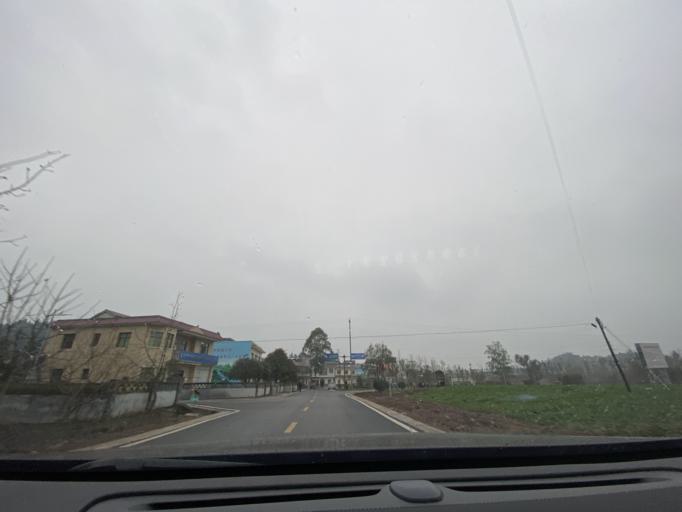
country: CN
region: Sichuan
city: Jiancheng
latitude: 30.3928
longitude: 104.6348
